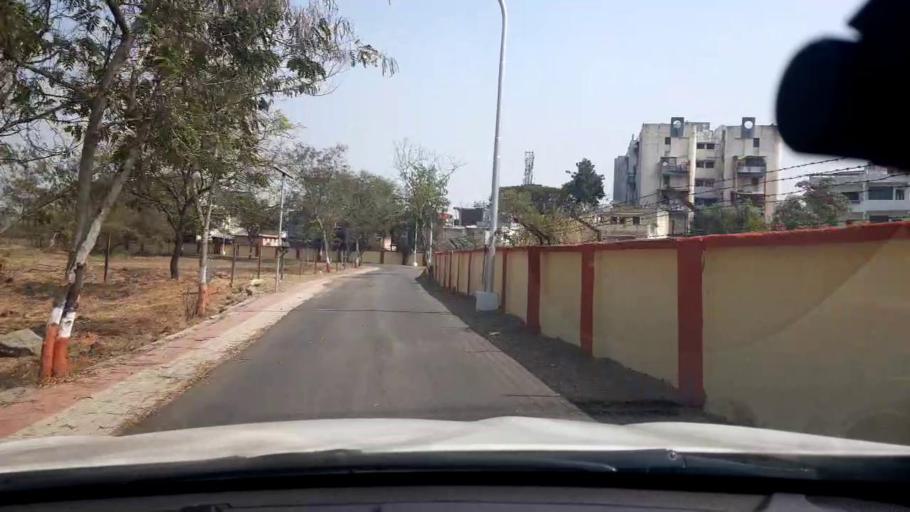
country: IN
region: Maharashtra
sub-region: Pune Division
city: Shivaji Nagar
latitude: 18.5417
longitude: 73.8635
